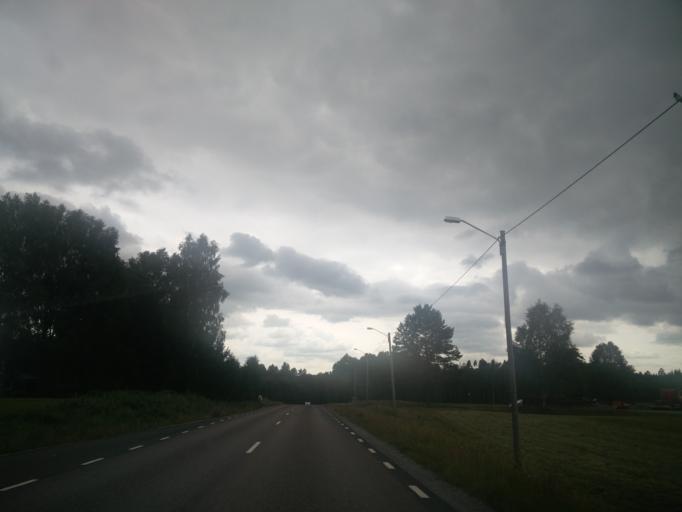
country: SE
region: Vaermland
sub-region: Arvika Kommun
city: Arvika
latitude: 59.8854
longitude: 12.6262
